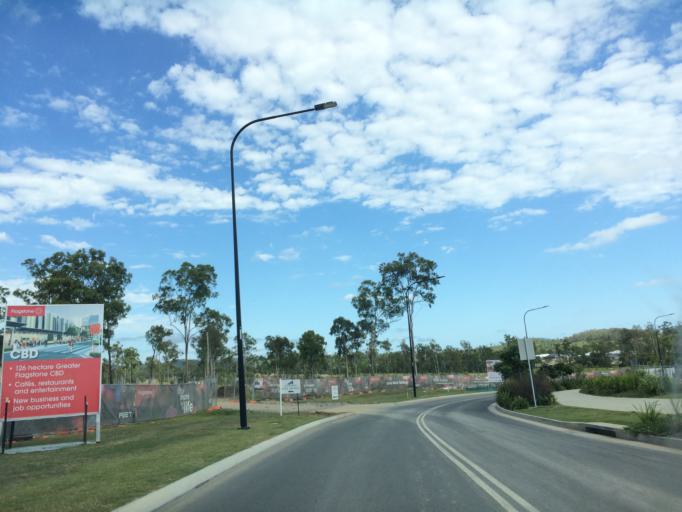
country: AU
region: Queensland
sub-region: Logan
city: North Maclean
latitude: -27.8072
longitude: 152.9467
